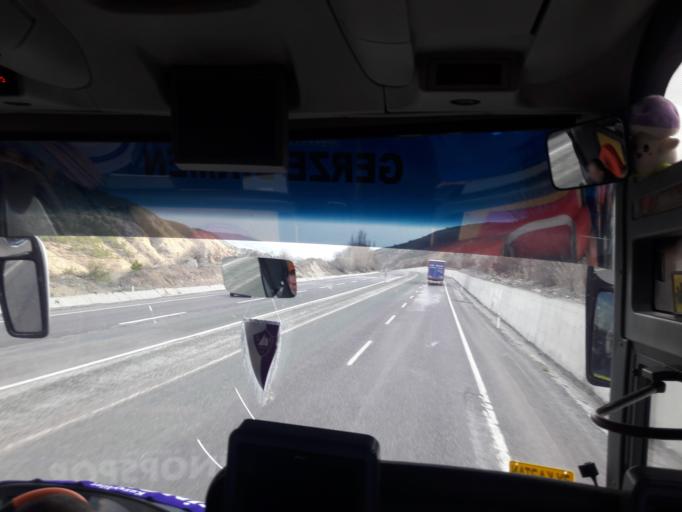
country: TR
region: Cankiri
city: Korgun
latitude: 40.7604
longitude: 33.5270
